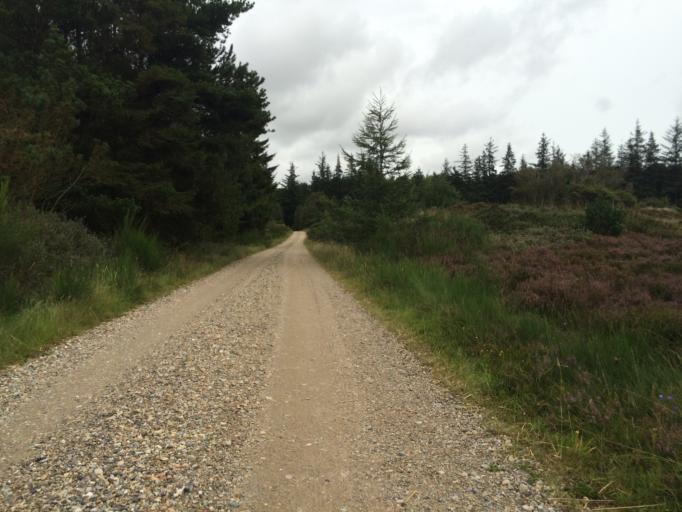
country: DK
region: Central Jutland
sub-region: Holstebro Kommune
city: Ulfborg
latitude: 56.2219
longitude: 8.4034
